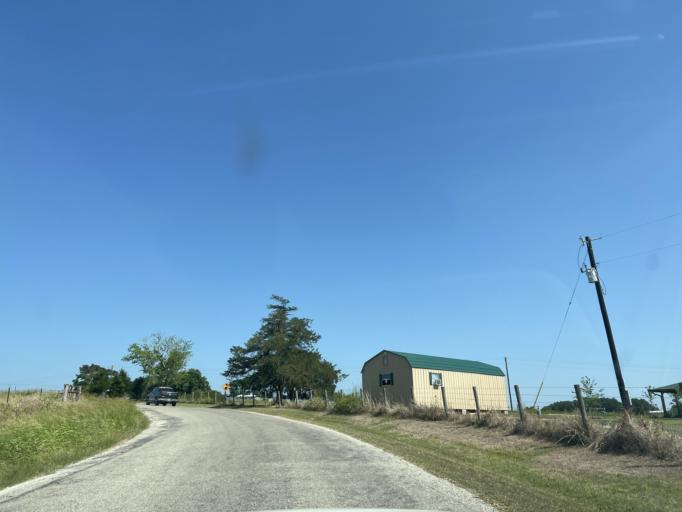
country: US
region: Texas
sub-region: Washington County
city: Brenham
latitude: 30.1637
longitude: -96.3278
